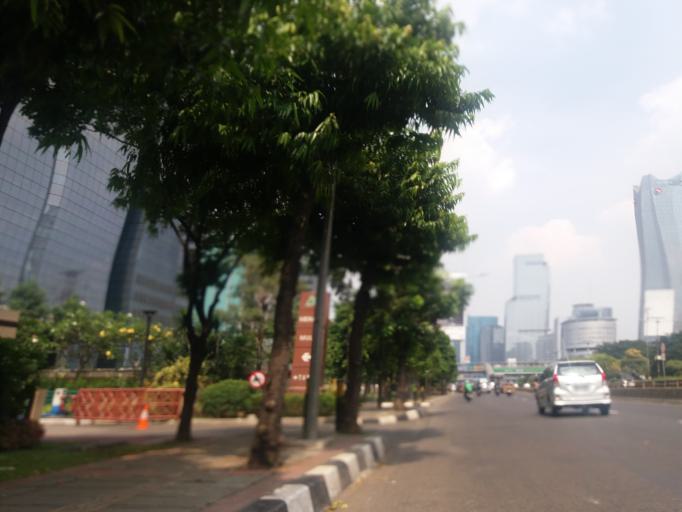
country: ID
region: Jakarta Raya
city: Jakarta
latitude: -6.2251
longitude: 106.8166
